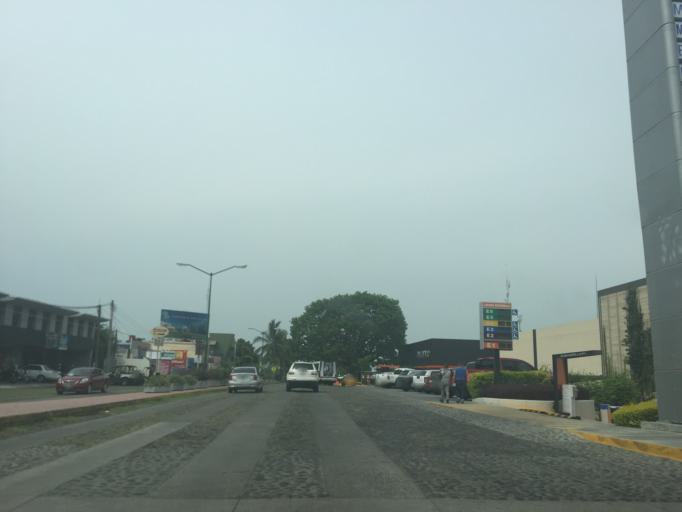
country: MX
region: Colima
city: Colima
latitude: 19.2530
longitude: -103.7196
